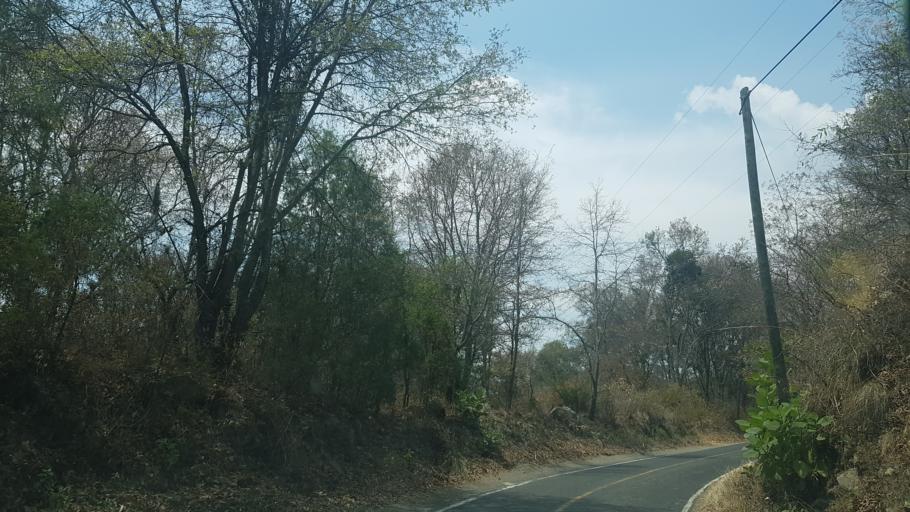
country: MX
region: Puebla
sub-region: Tochimilco
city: La Magdalena Yancuitlalpan
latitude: 18.8825
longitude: -98.5934
